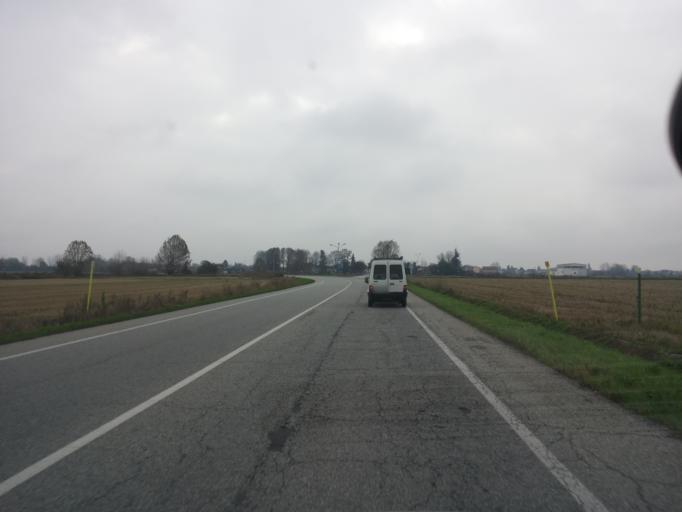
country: IT
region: Piedmont
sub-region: Provincia di Vercelli
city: Stroppiana
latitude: 45.2404
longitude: 8.4574
